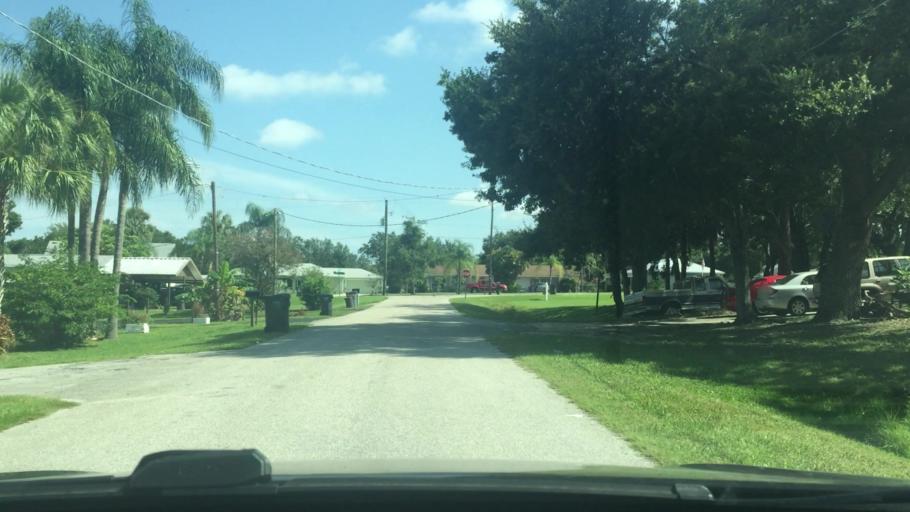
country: US
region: Florida
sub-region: Hillsborough County
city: Ruskin
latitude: 27.6943
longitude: -82.4447
